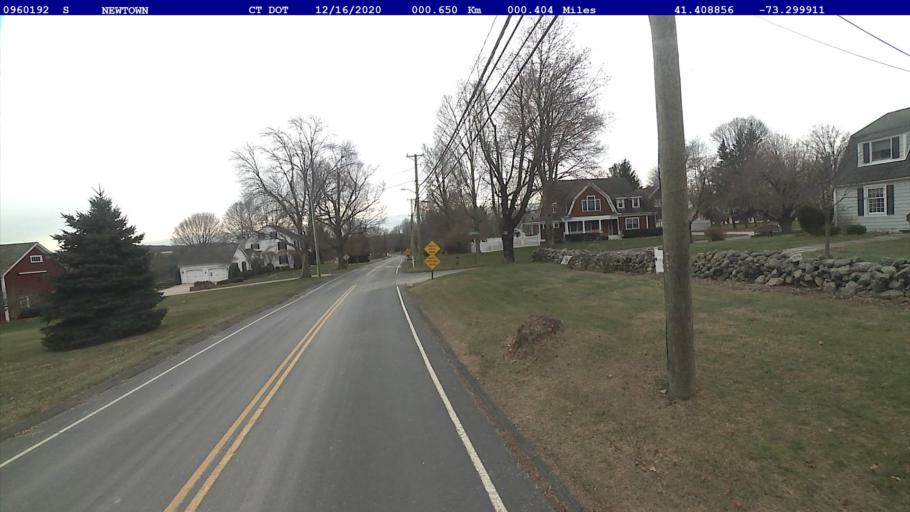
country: US
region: Connecticut
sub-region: Fairfield County
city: Newtown
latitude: 41.4088
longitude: -73.2999
